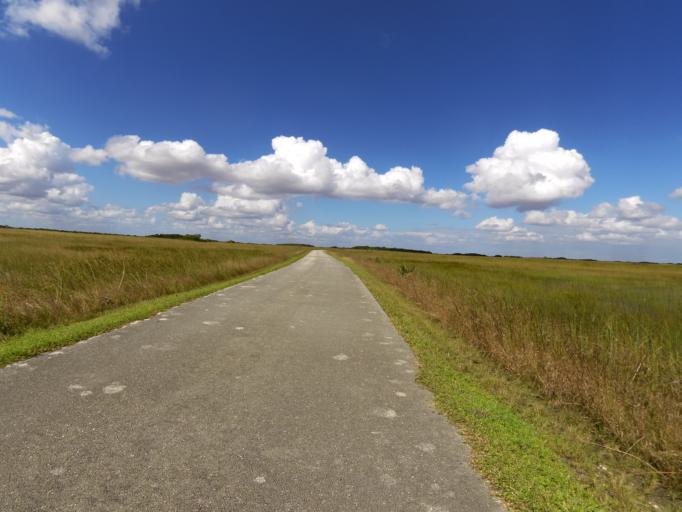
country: US
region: Florida
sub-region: Miami-Dade County
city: The Hammocks
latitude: 25.6658
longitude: -80.7614
